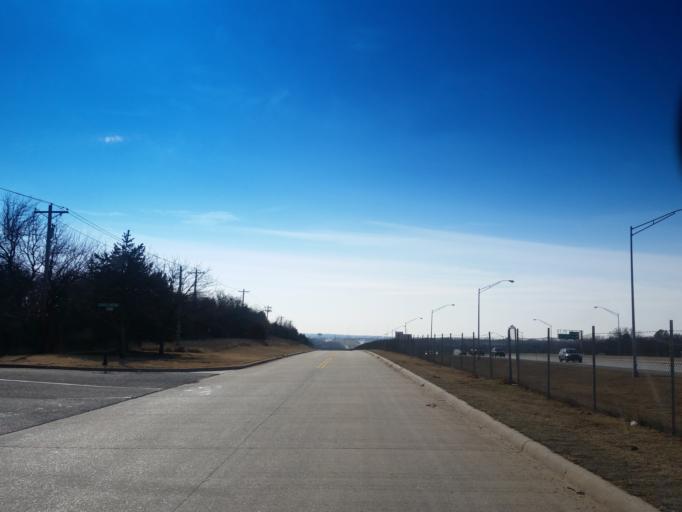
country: US
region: Oklahoma
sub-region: Oklahoma County
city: Edmond
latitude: 35.6302
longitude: -97.4244
